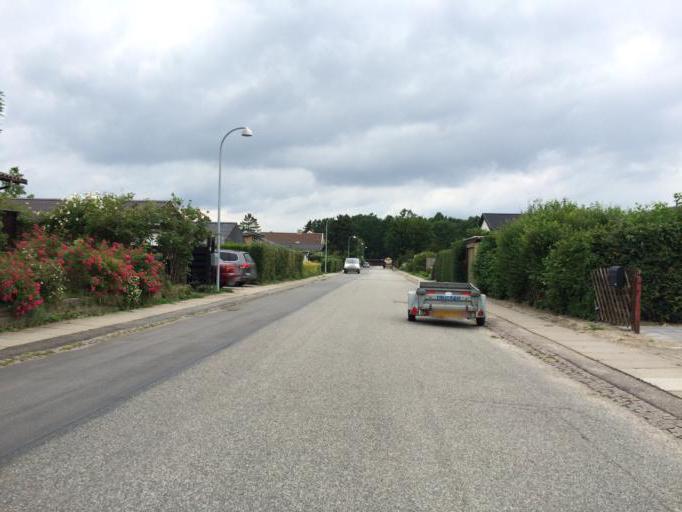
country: DK
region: Capital Region
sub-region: Hvidovre Kommune
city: Hvidovre
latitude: 55.6213
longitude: 12.4813
